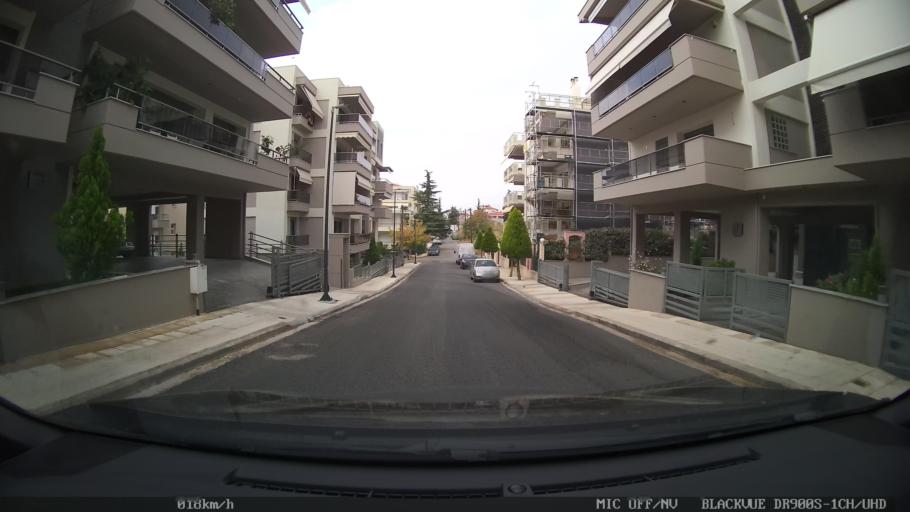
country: GR
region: Central Macedonia
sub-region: Nomos Thessalonikis
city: Pylaia
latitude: 40.6101
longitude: 22.9964
